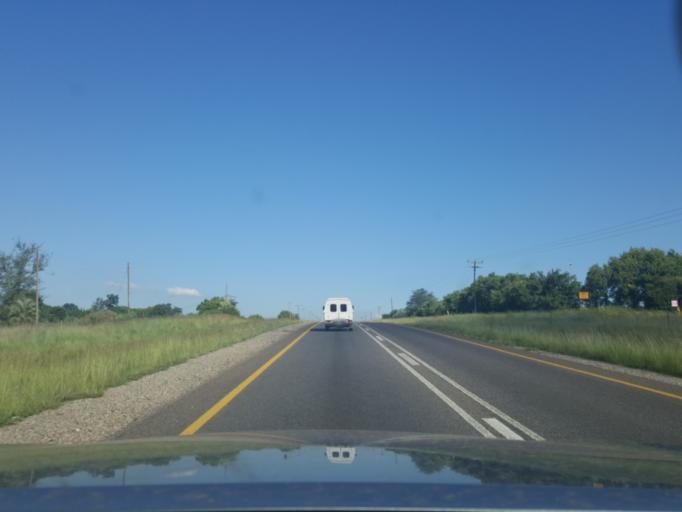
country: ZA
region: Gauteng
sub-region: City of Tshwane Metropolitan Municipality
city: Cullinan
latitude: -25.7877
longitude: 28.5089
